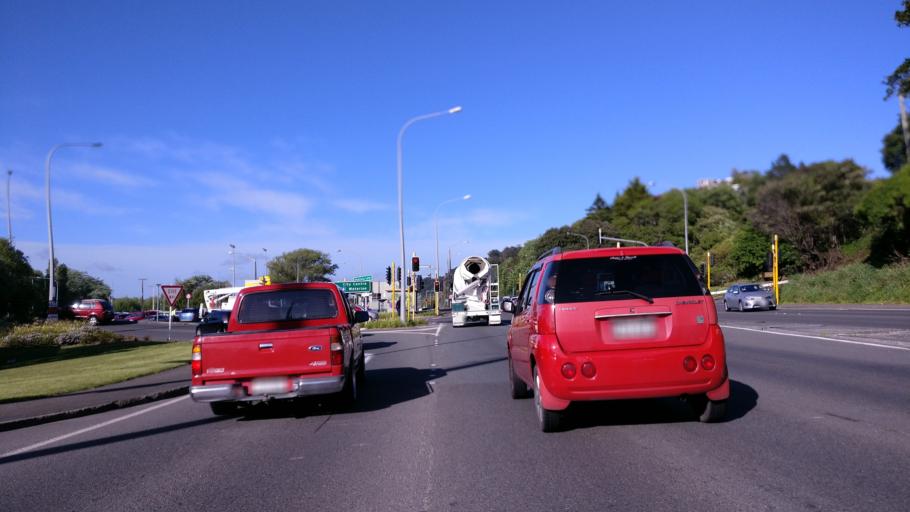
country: NZ
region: Wellington
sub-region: Lower Hutt City
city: Lower Hutt
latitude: -41.2029
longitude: 174.9066
